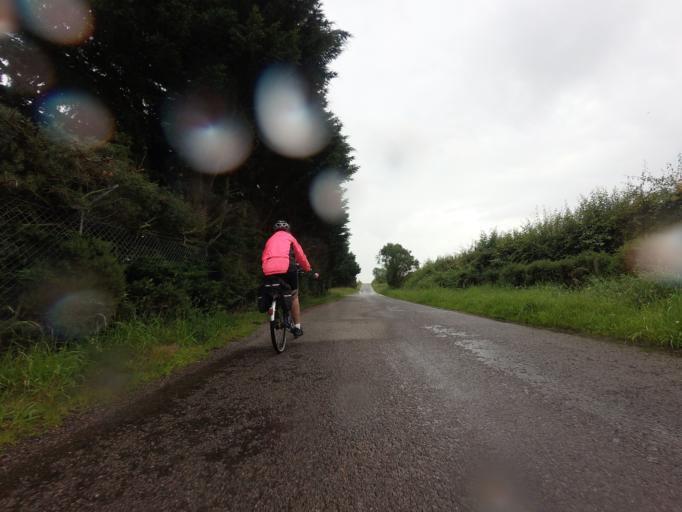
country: GB
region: Scotland
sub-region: Moray
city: Fochabers
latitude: 57.6640
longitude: -3.0731
